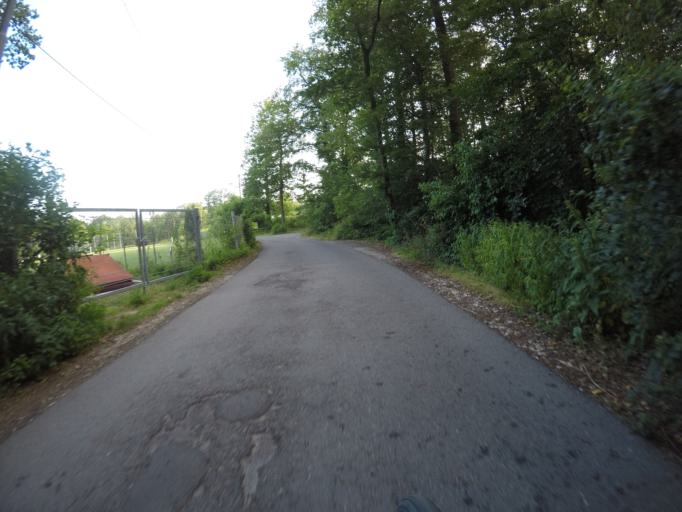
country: DE
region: Baden-Wuerttemberg
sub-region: Regierungsbezirk Stuttgart
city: Stuttgart-Ost
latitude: 48.7728
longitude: 9.2199
